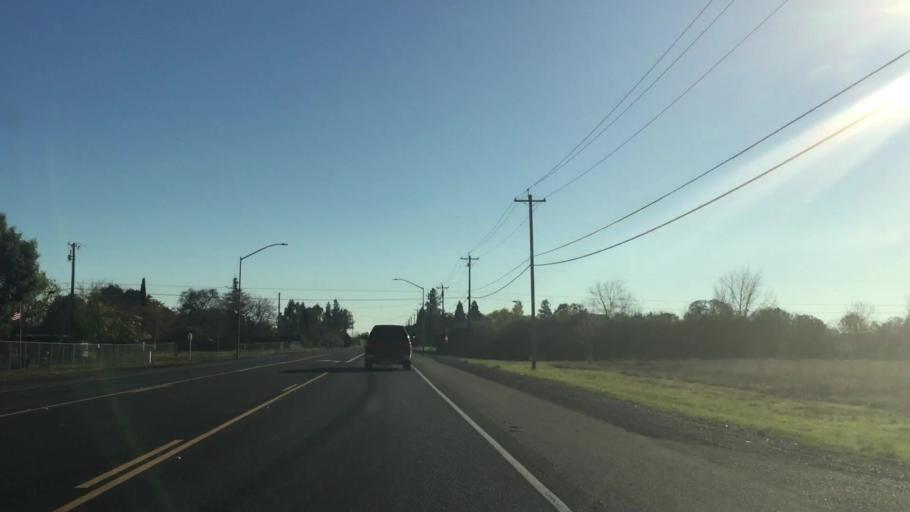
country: US
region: California
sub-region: Butte County
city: Palermo
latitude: 39.4298
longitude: -121.6052
